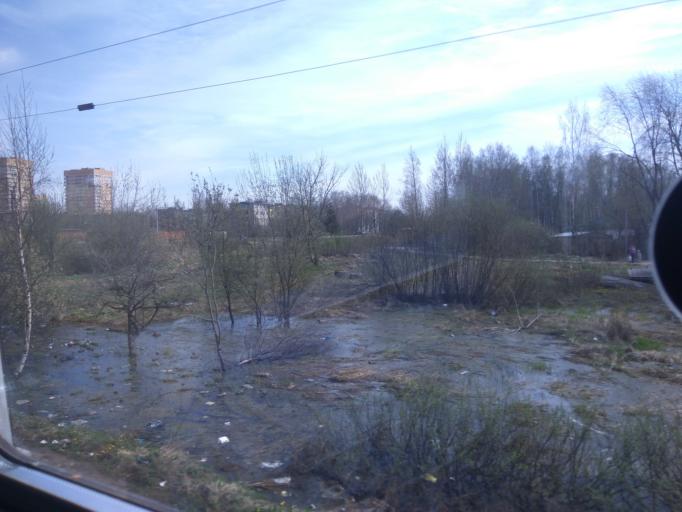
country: RU
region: Moskovskaya
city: Lobnya
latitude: 56.0214
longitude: 37.4849
